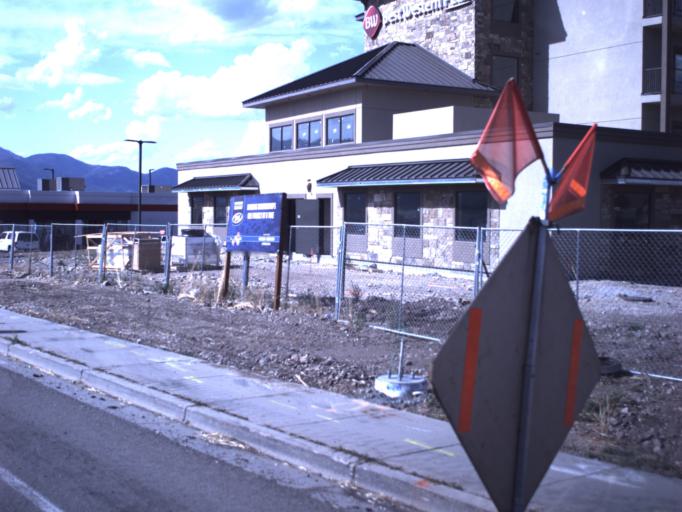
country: US
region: Utah
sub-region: Wasatch County
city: Heber
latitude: 40.4917
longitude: -111.4120
